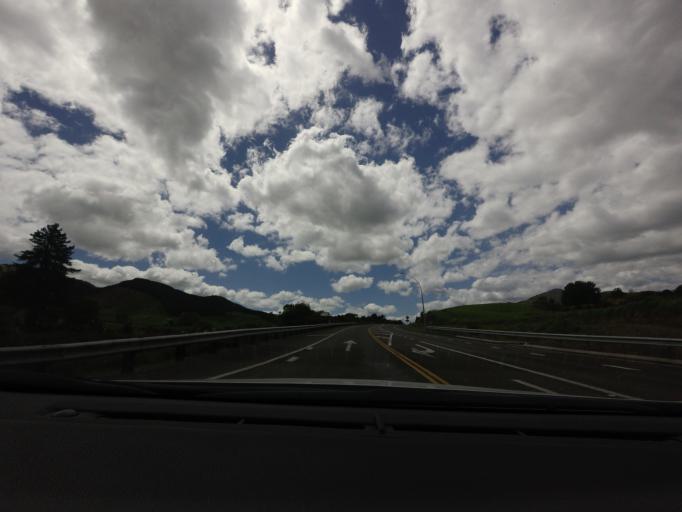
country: NZ
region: Bay of Plenty
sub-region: Rotorua District
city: Rotorua
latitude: -38.3392
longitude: 176.3638
